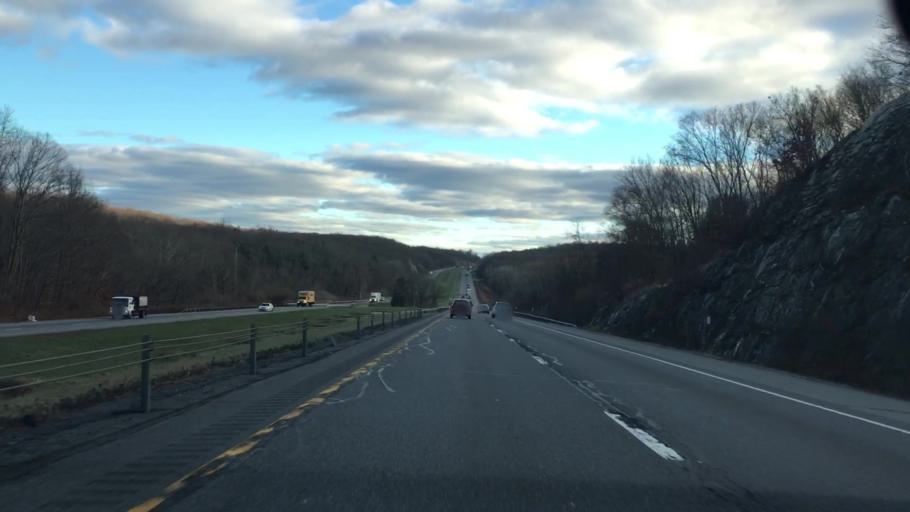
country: US
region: New York
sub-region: Putnam County
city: Lake Carmel
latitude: 41.4535
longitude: -73.6398
